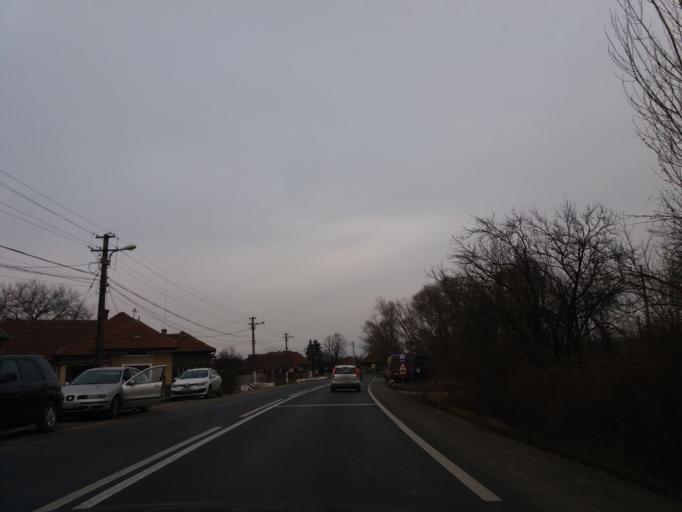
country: RO
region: Hunedoara
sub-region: Comuna Bacia
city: Bacia
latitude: 45.7729
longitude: 23.0022
